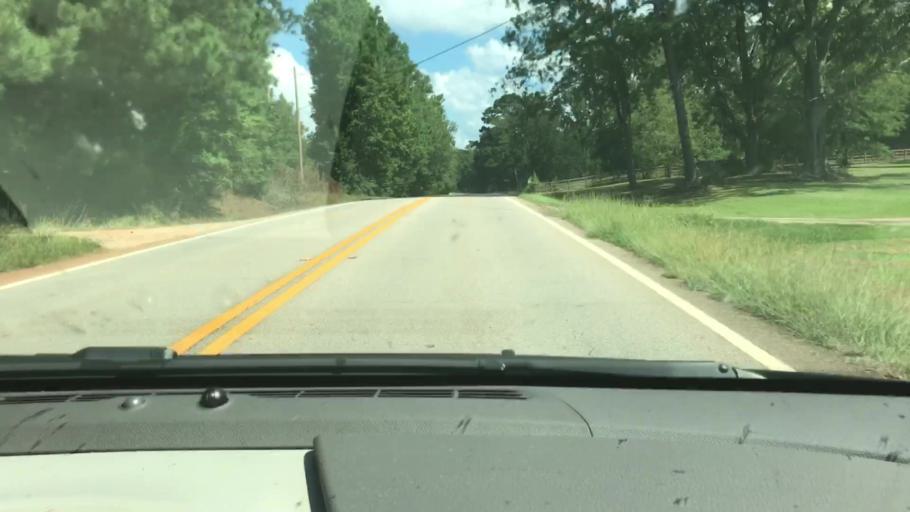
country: US
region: Georgia
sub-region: Troup County
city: La Grange
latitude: 32.9379
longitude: -85.0189
